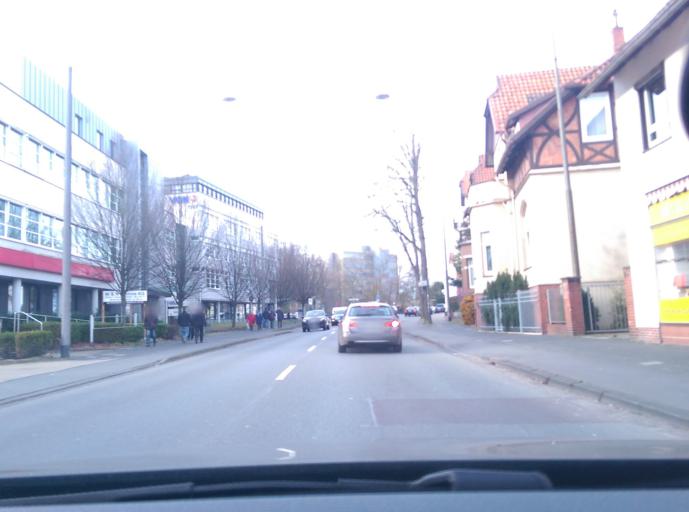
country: DE
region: Lower Saxony
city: Celle
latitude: 52.6163
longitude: 10.0777
